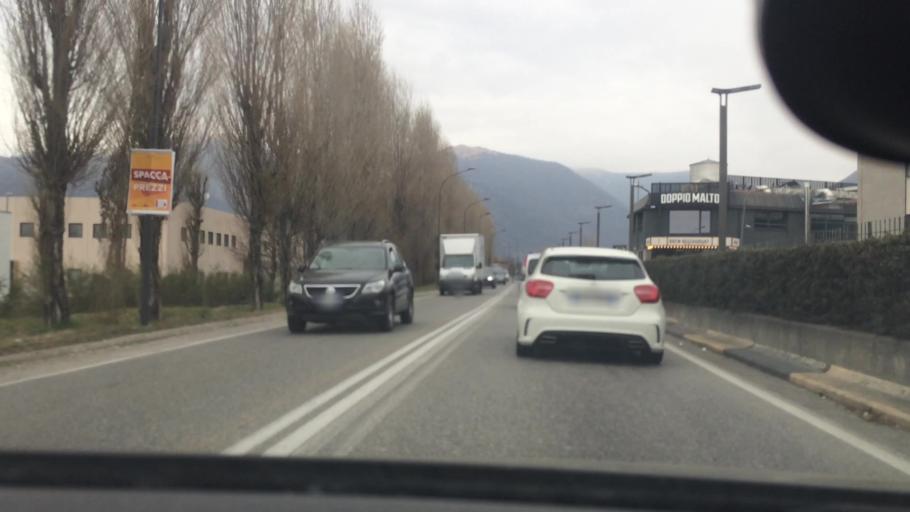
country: IT
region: Lombardy
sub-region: Provincia di Como
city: Merone
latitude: 45.7994
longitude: 9.2387
